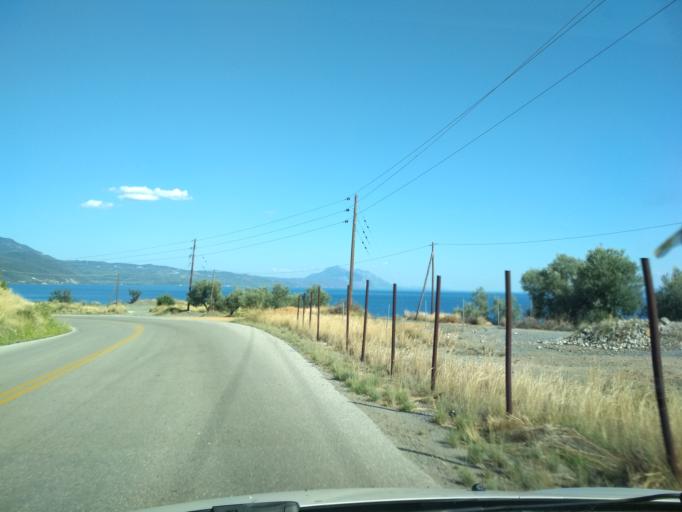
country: GR
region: Central Greece
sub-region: Nomos Evvoias
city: Oreoi
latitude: 38.8417
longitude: 23.0982
